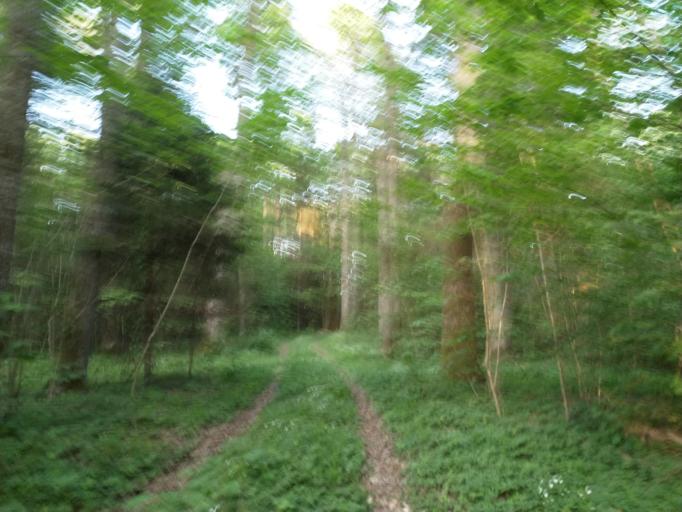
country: LV
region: Aizpute
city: Aizpute
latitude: 56.8276
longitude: 21.7726
